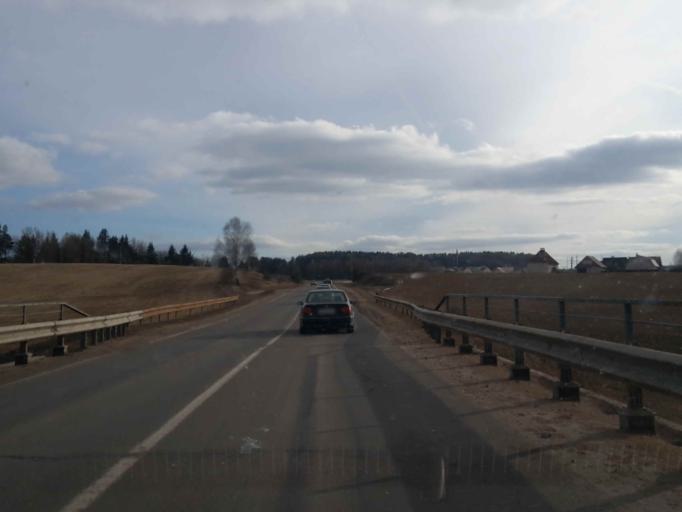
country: BY
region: Minsk
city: Bal'shavik
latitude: 54.0361
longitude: 27.5609
